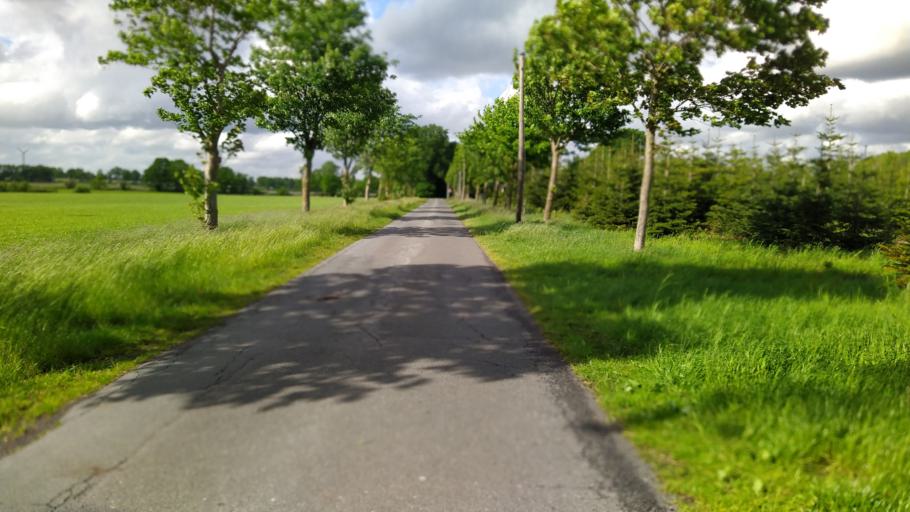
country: DE
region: Lower Saxony
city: Brest
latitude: 53.4564
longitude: 9.3921
